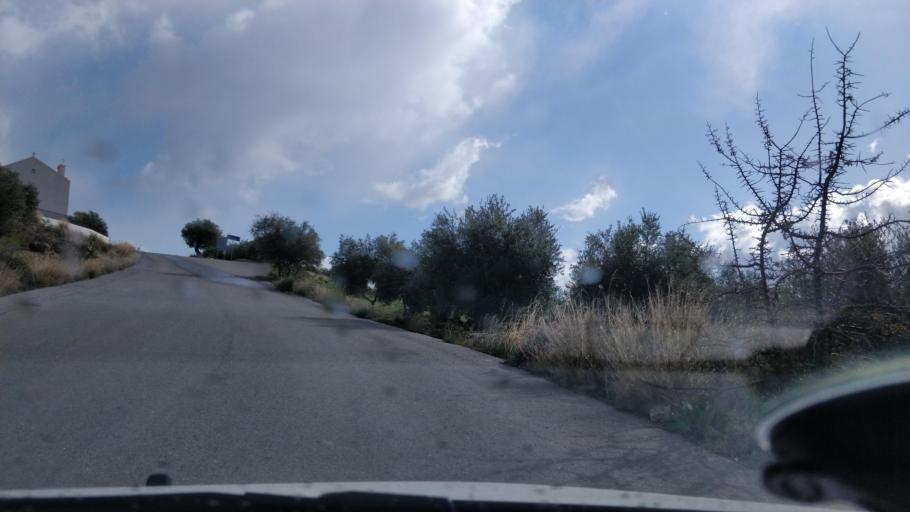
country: GR
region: Crete
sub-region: Nomos Lasithiou
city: Gra Liyia
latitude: 34.9983
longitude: 25.5135
